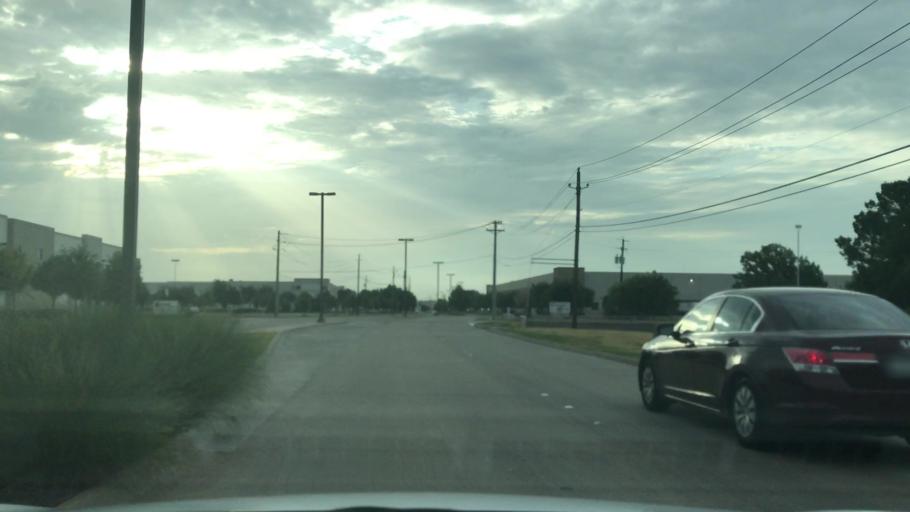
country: US
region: Texas
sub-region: Dallas County
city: Coppell
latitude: 32.9550
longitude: -97.0181
